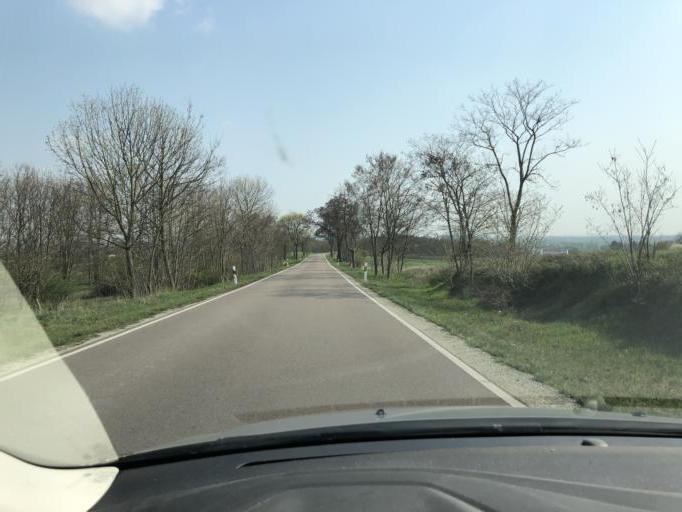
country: DE
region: Saxony-Anhalt
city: Niemberg
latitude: 51.5559
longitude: 12.0765
